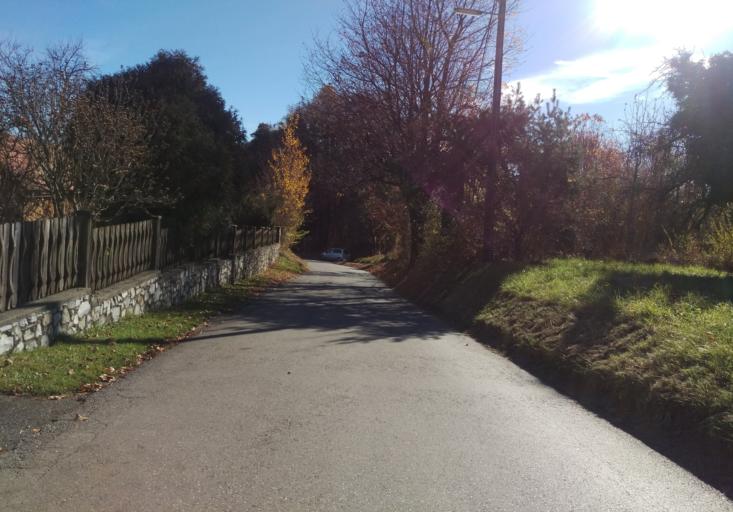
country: AT
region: Styria
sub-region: Graz Stadt
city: Mariatrost
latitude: 47.1220
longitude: 15.4912
